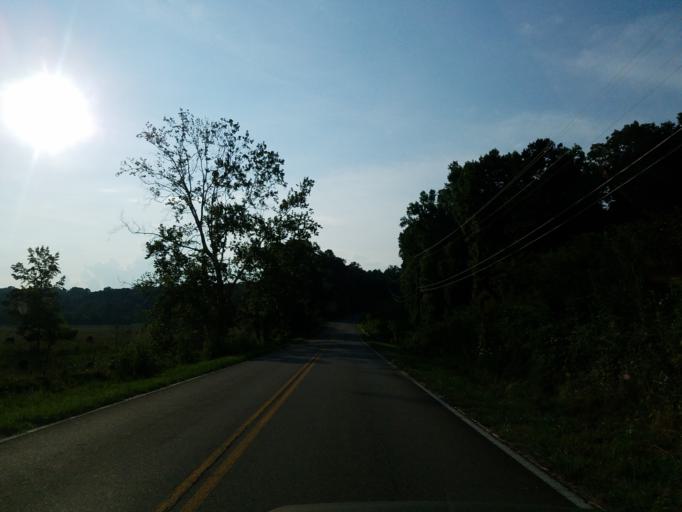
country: US
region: Georgia
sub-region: Pickens County
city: Jasper
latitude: 34.5259
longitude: -84.5259
